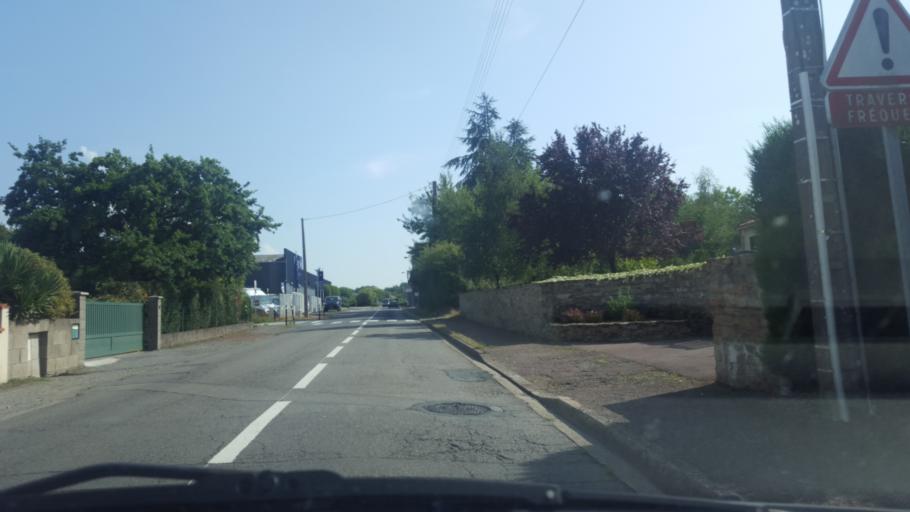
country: FR
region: Pays de la Loire
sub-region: Departement de la Loire-Atlantique
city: Saint-Philbert-de-Grand-Lieu
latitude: 47.0303
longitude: -1.6352
